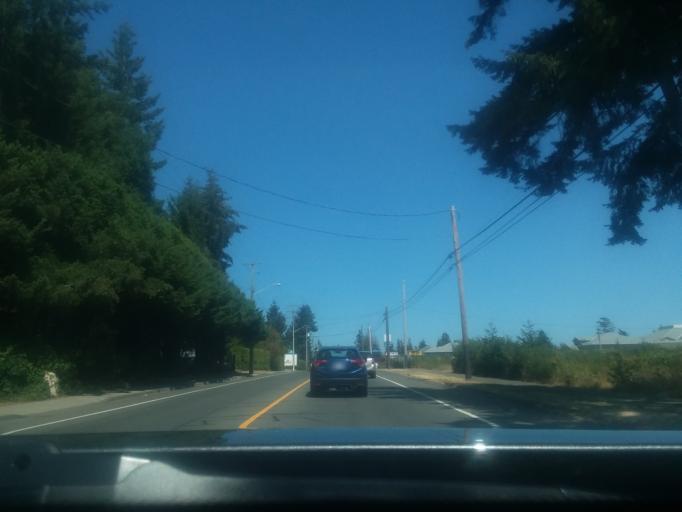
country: CA
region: British Columbia
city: Courtenay
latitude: 49.6853
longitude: -124.9350
